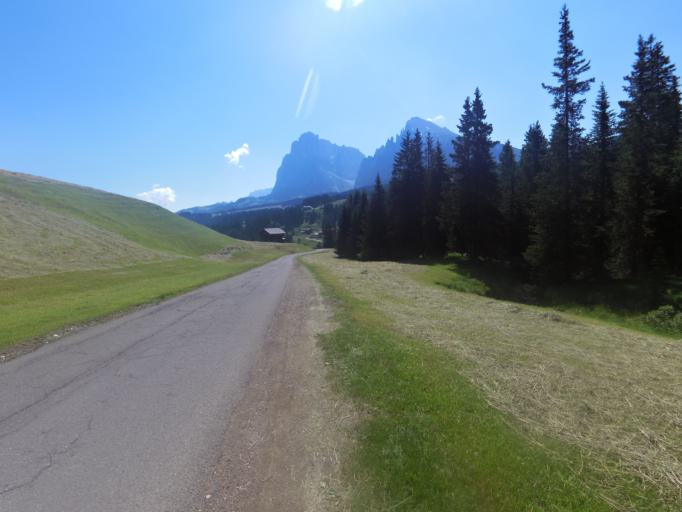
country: IT
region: Trentino-Alto Adige
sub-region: Bolzano
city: Ortisei
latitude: 46.5319
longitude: 11.6658
